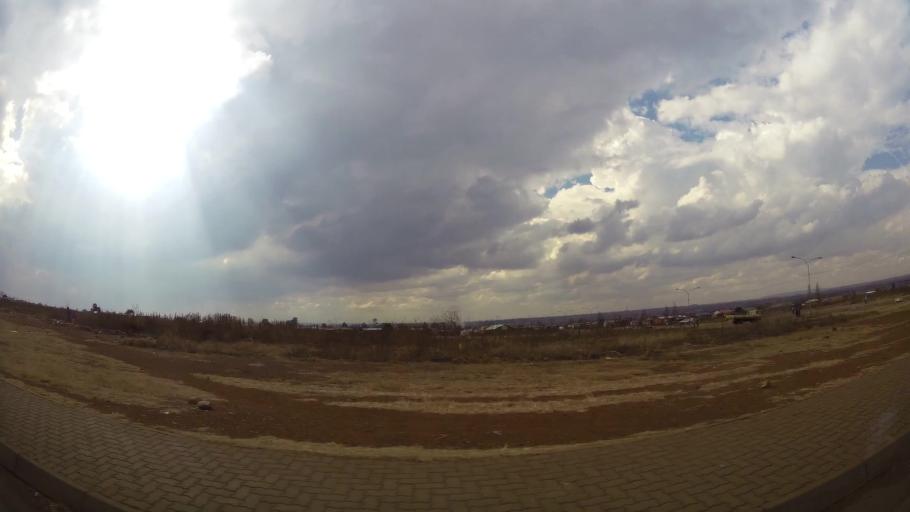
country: ZA
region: Gauteng
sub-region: Ekurhuleni Metropolitan Municipality
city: Germiston
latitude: -26.3959
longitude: 28.1575
